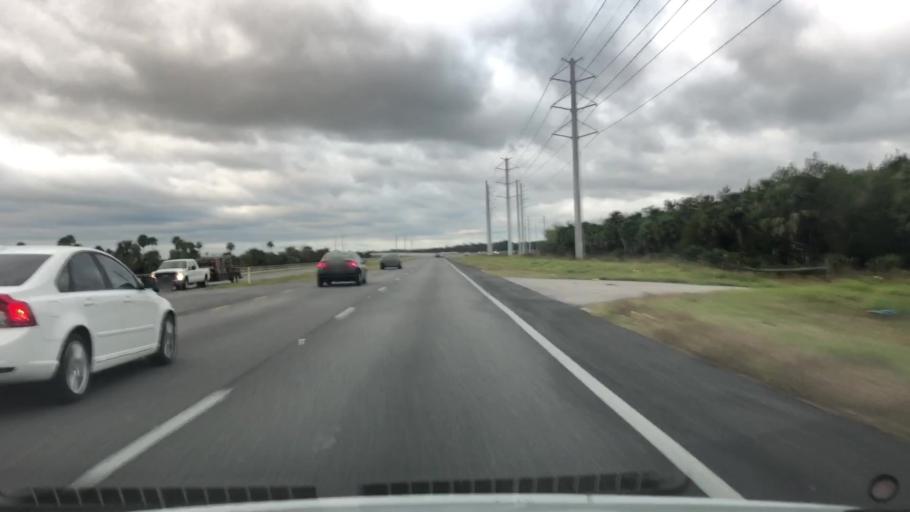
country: US
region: Florida
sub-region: Seminole County
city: Midway
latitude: 28.8106
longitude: -81.1985
